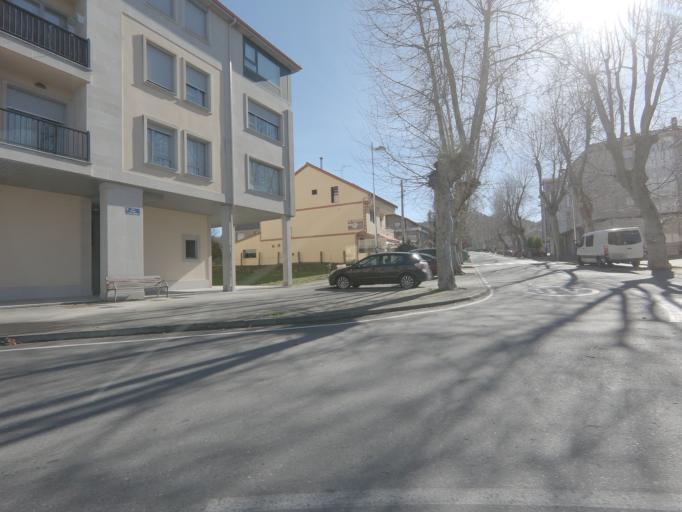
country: ES
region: Galicia
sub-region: Provincia de Ourense
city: Allariz
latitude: 42.1858
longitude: -7.7969
